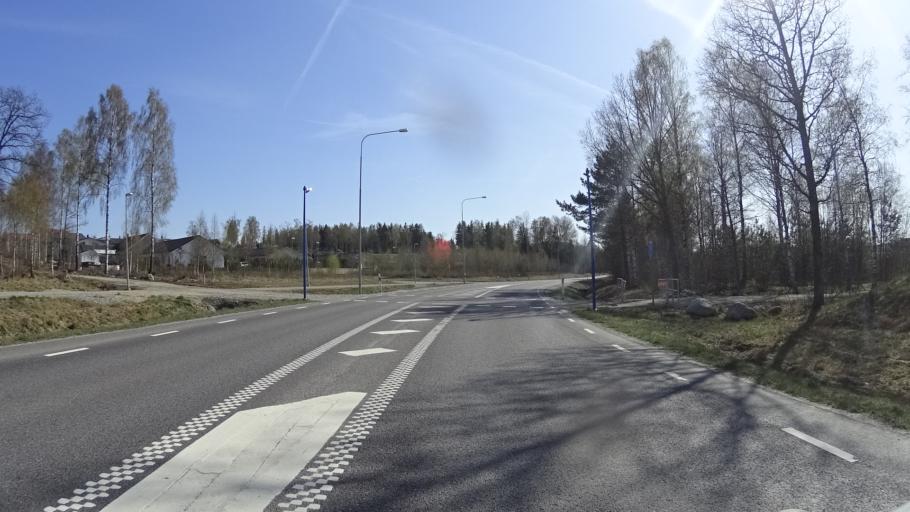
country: SE
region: Kronoberg
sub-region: Ljungby Kommun
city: Ljungby
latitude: 56.8404
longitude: 13.9745
